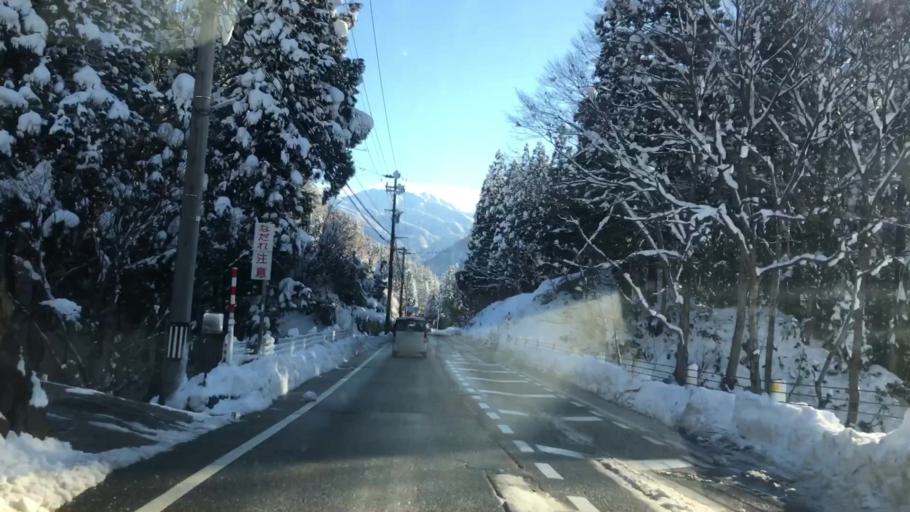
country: JP
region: Toyama
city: Kamiichi
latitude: 36.5824
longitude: 137.3973
